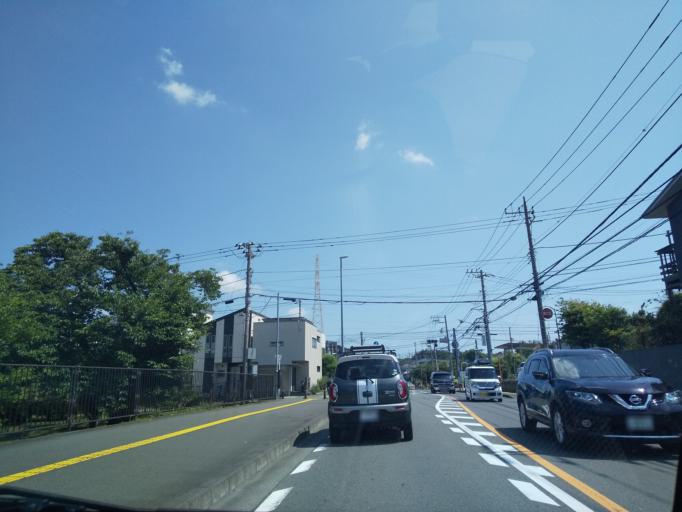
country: JP
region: Kanagawa
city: Zama
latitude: 35.4919
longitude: 139.4064
